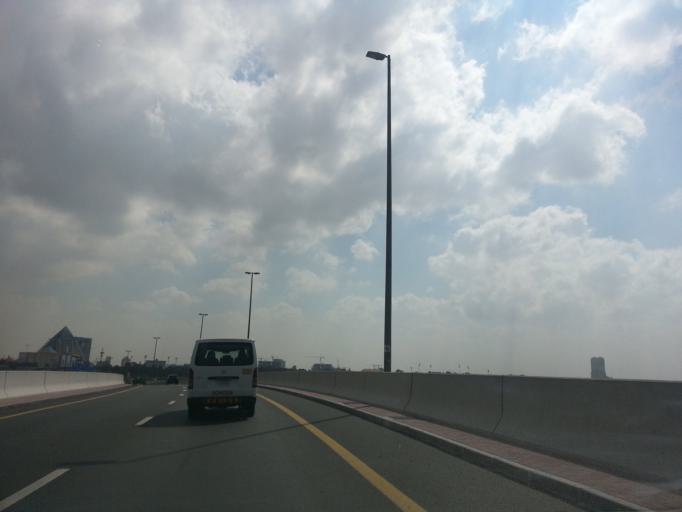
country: AE
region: Ash Shariqah
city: Sharjah
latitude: 25.2323
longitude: 55.3076
